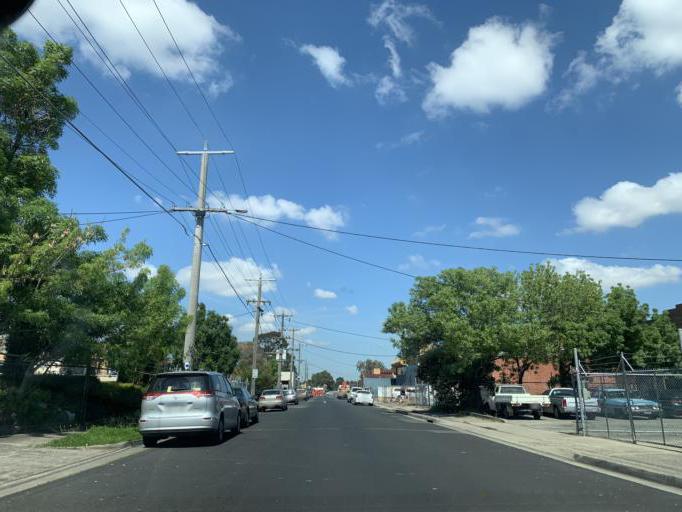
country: AU
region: Victoria
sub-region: Moreland
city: Coburg North
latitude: -37.7312
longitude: 144.9527
